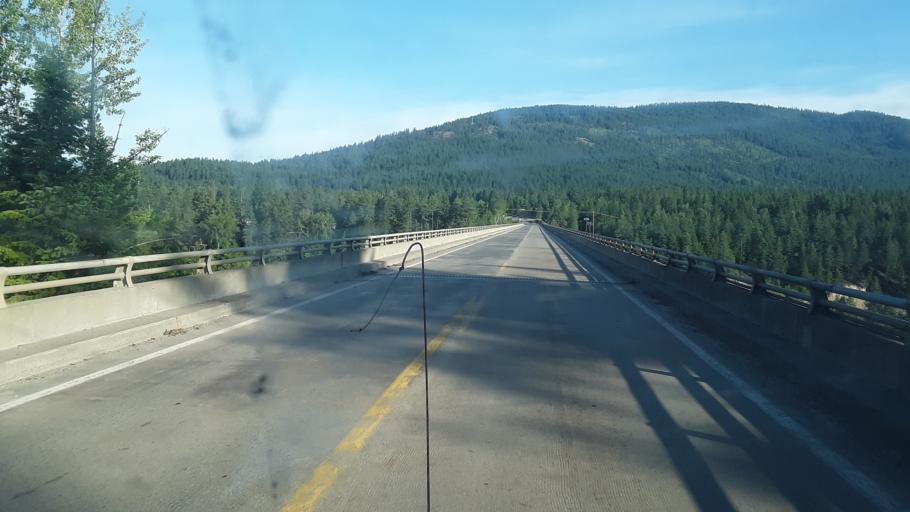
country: US
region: Idaho
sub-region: Boundary County
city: Bonners Ferry
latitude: 48.7275
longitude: -116.1764
